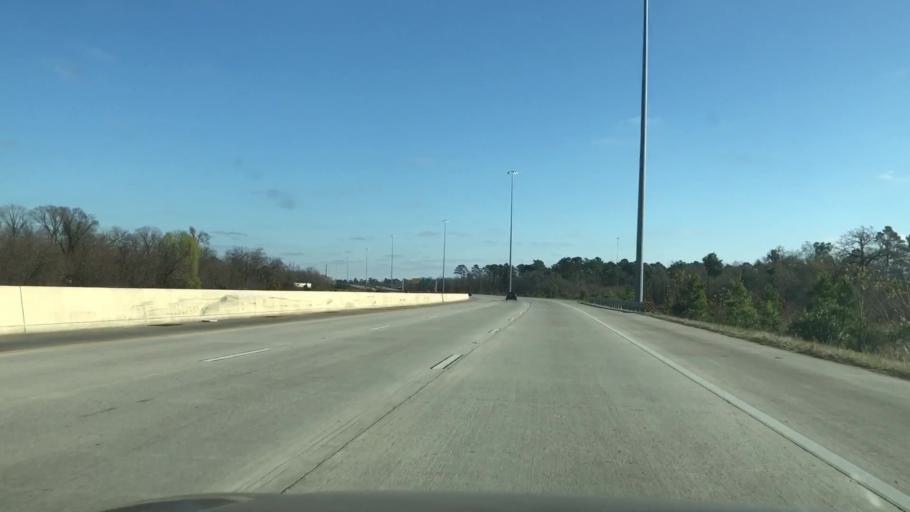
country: US
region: Texas
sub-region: Harris County
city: Jacinto City
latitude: 29.7944
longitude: -95.2296
